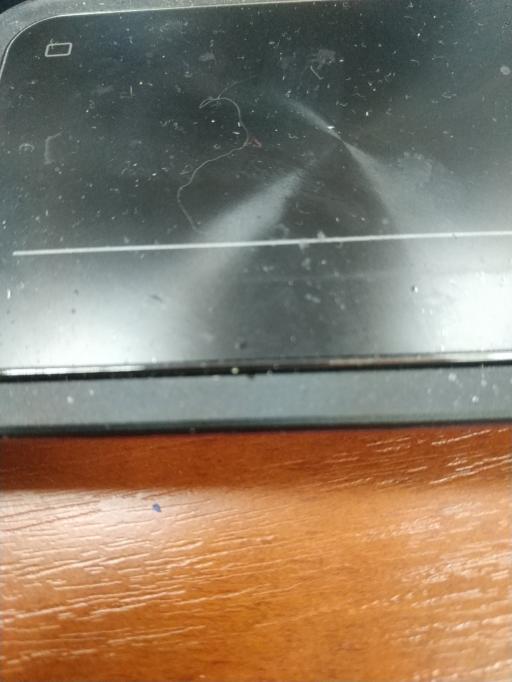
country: RU
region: Tula
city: Zaokskiy
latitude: 54.7272
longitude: 37.4972
